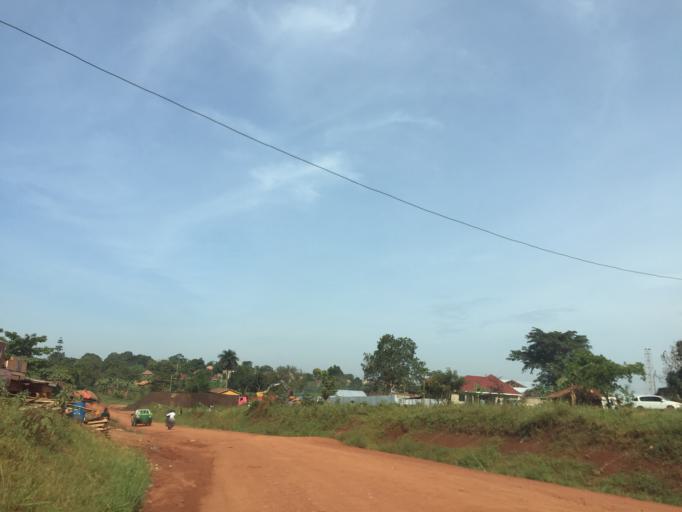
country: UG
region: Central Region
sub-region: Wakiso District
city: Wakiso
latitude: 0.4638
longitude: 32.5543
